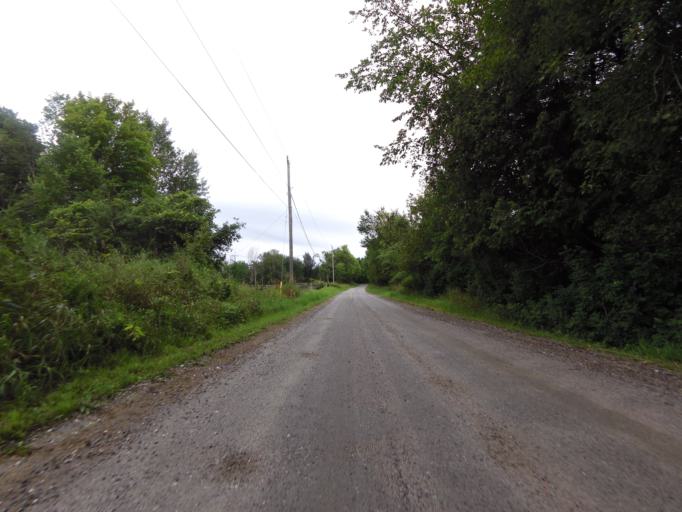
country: CA
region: Ontario
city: Perth
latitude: 45.0504
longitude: -76.3946
